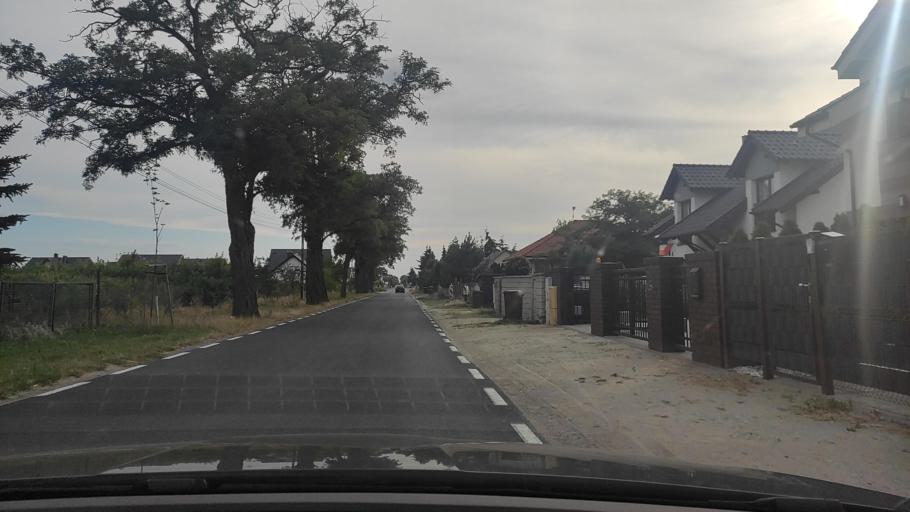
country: PL
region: Greater Poland Voivodeship
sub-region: Powiat poznanski
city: Kleszczewo
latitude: 52.3693
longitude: 17.1467
